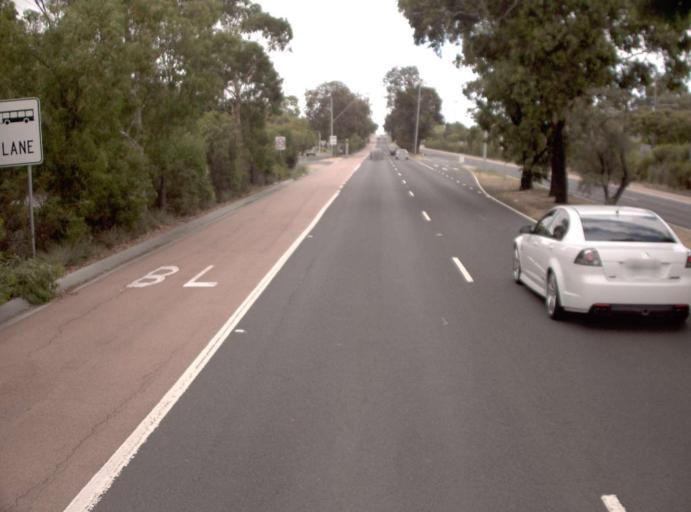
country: AU
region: Victoria
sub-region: Knox
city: Scoresby
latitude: -37.8944
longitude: 145.2329
